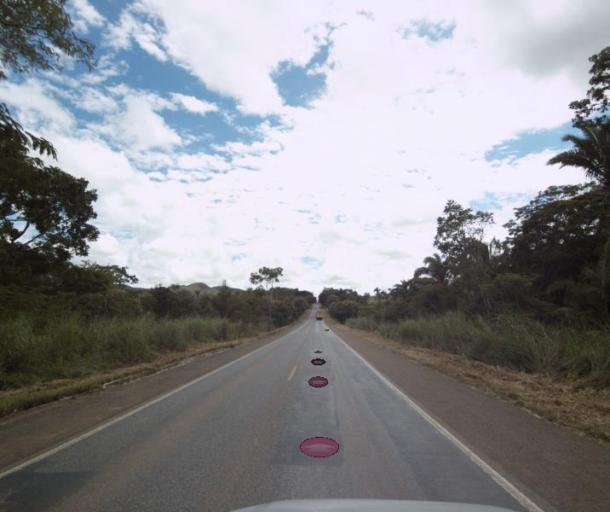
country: BR
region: Goias
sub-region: Uruacu
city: Uruacu
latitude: -14.4167
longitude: -49.1572
